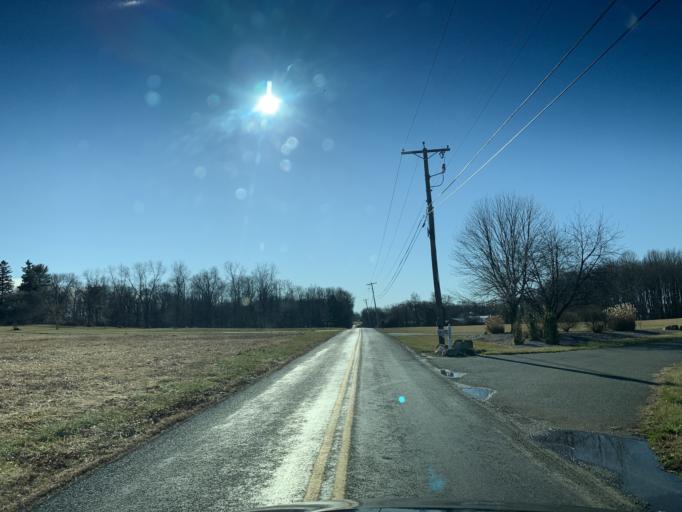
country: US
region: Maryland
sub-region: Harford County
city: Riverside
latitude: 39.5410
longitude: -76.2349
